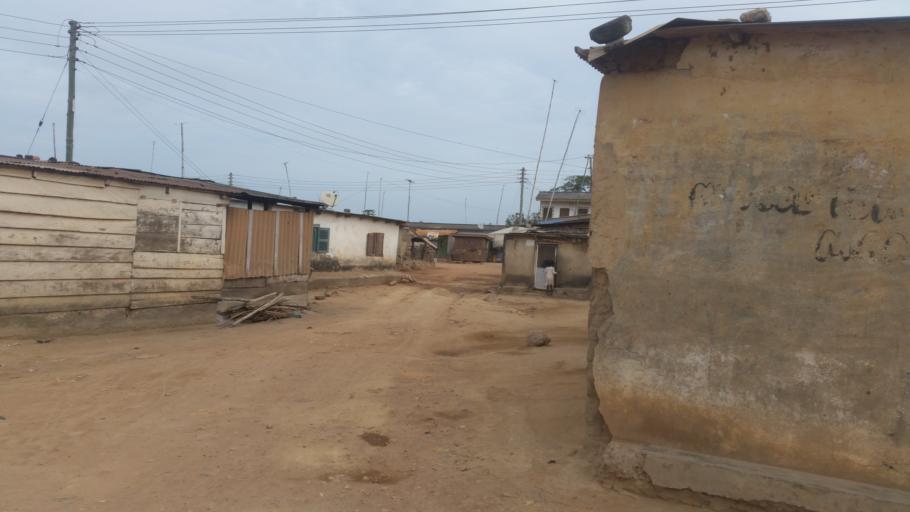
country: GH
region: Central
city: Cape Coast
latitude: 5.1247
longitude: -1.3006
